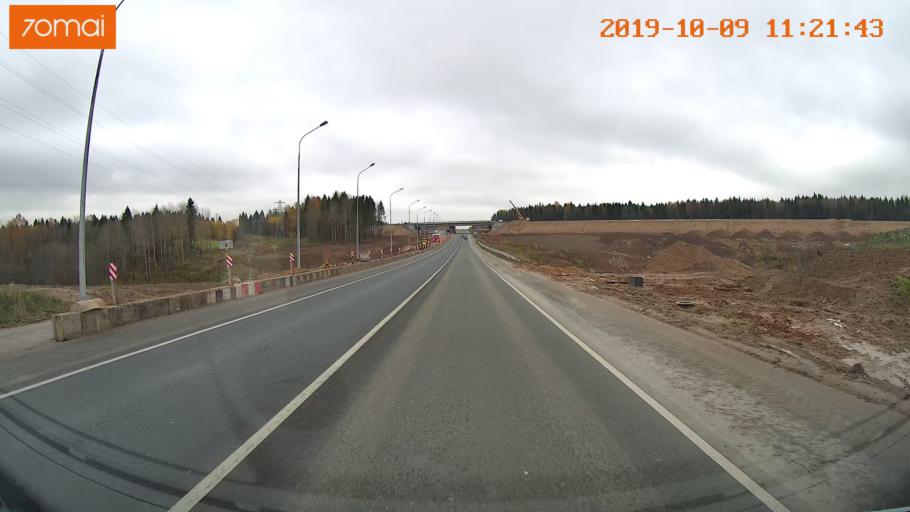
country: RU
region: Vologda
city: Vologda
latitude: 59.1373
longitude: 39.9518
